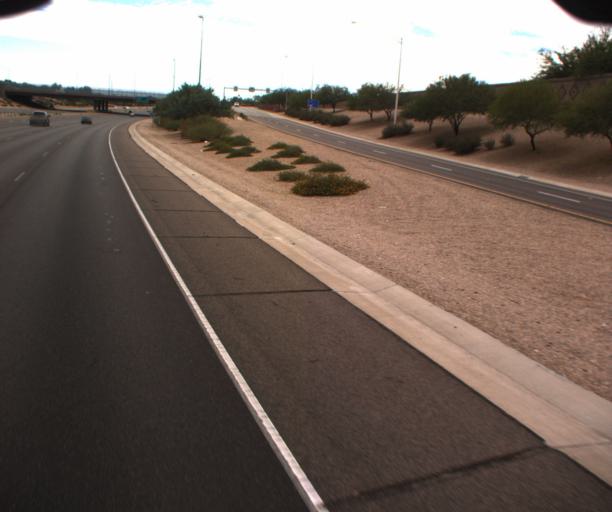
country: US
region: Arizona
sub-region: Pinal County
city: Apache Junction
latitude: 33.3675
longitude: -111.6447
